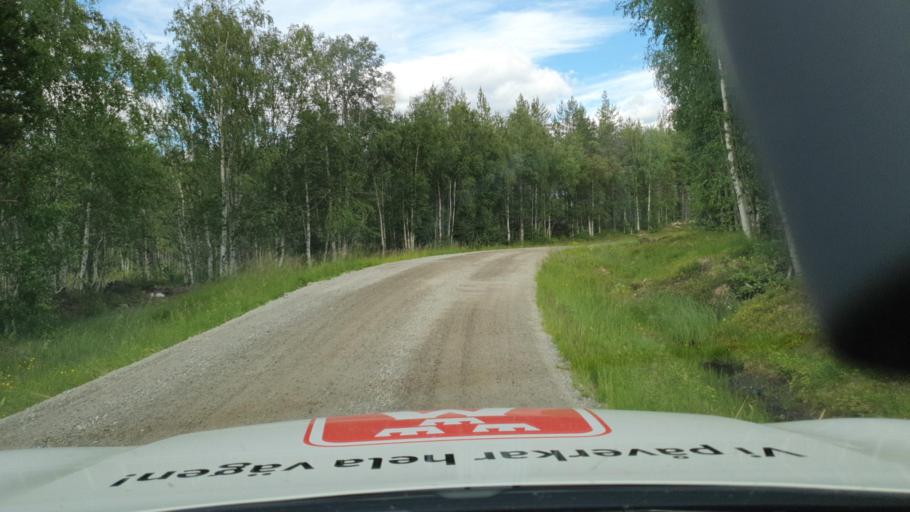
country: SE
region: Vaesterbotten
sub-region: Lycksele Kommun
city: Soderfors
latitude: 64.2626
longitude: 18.0877
